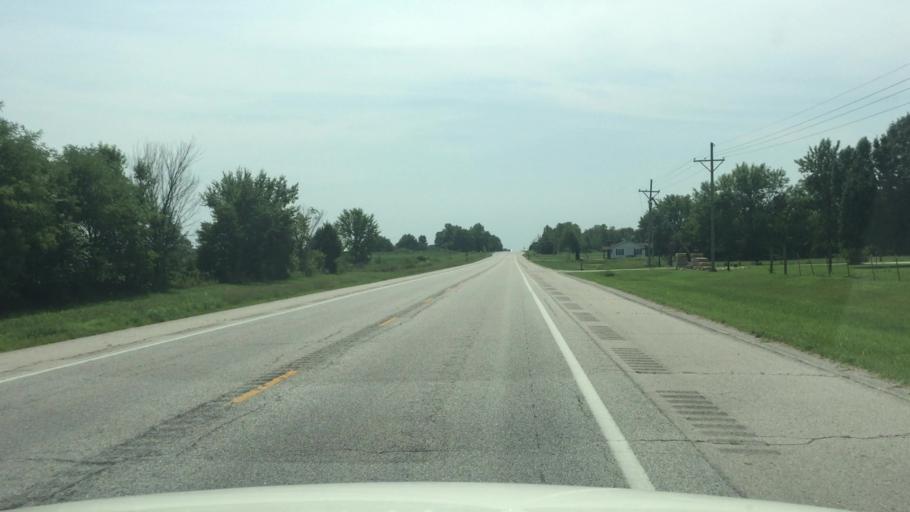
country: US
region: Kansas
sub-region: Cherokee County
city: Galena
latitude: 37.1096
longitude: -94.7044
